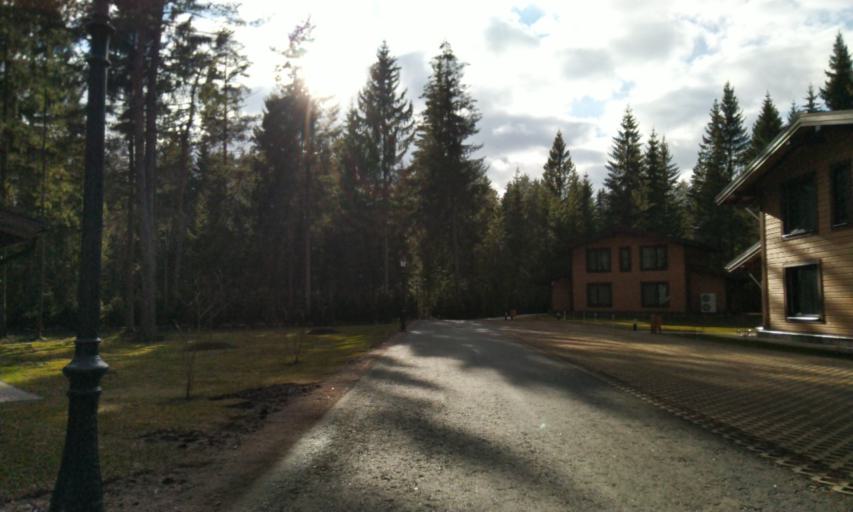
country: RU
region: Leningrad
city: Toksovo
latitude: 60.1313
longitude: 30.4497
